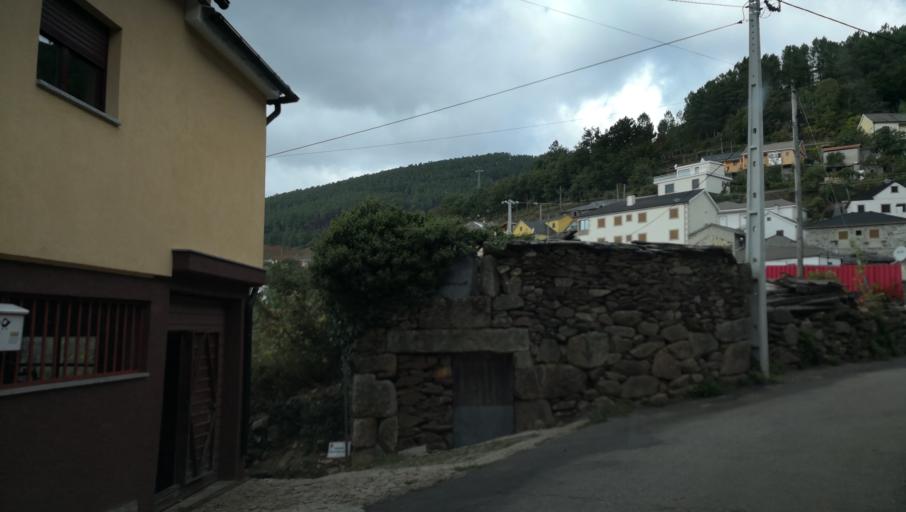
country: PT
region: Vila Real
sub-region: Vila Real
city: Vila Real
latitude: 41.3648
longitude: -7.8396
